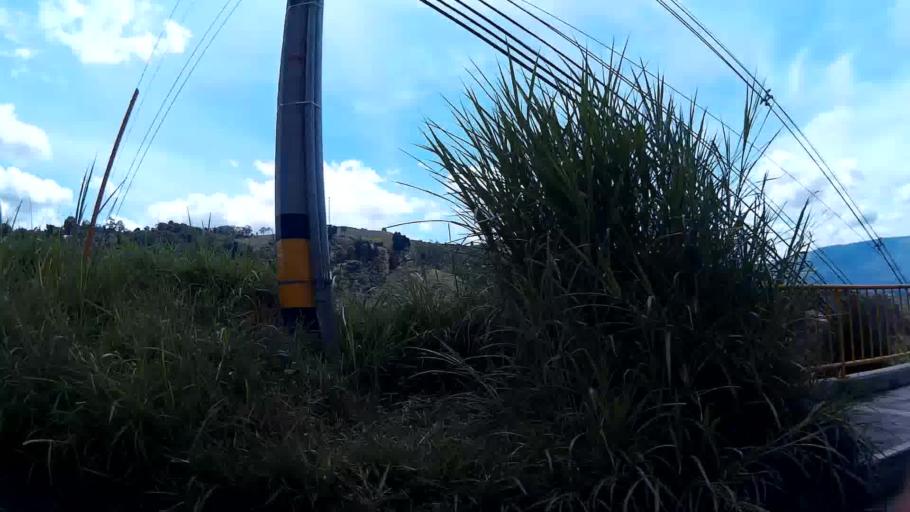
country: CO
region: Antioquia
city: Medellin
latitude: 6.2646
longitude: -75.6258
